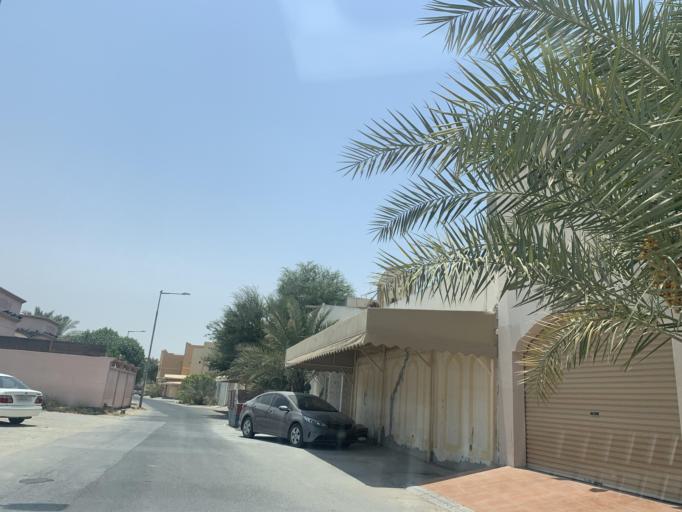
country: BH
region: Manama
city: Jidd Hafs
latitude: 26.2090
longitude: 50.4732
